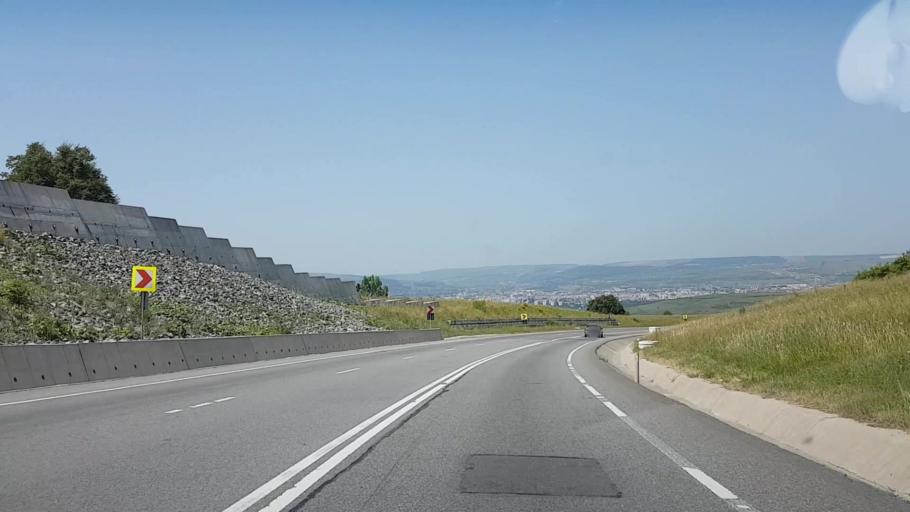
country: RO
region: Cluj
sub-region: Comuna Feleacu
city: Feleacu
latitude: 46.7236
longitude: 23.6459
